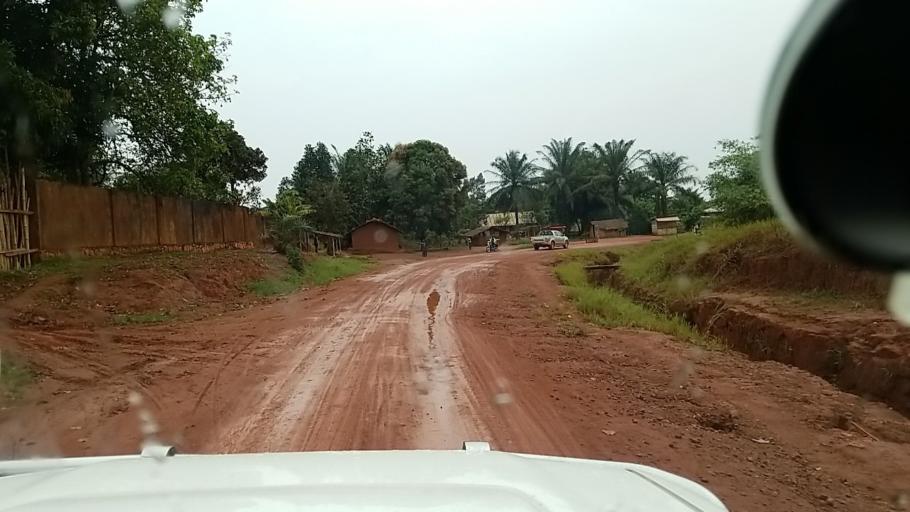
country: CD
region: Equateur
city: Gemena
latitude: 3.2345
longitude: 19.7815
